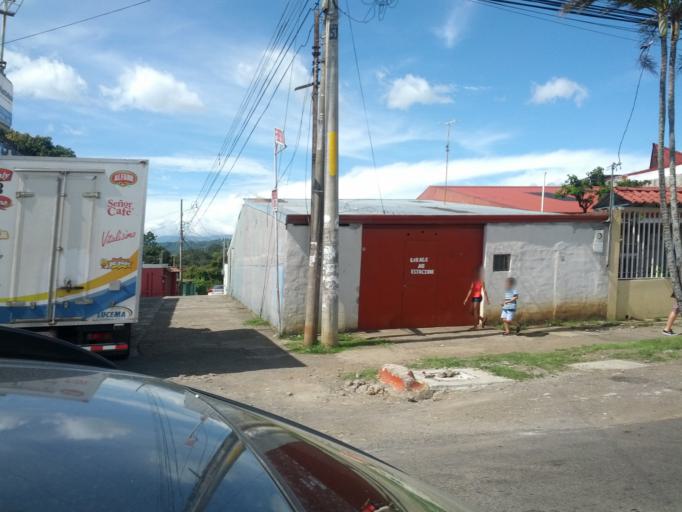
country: CR
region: Alajuela
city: Alajuela
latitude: 10.0266
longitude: -84.1839
